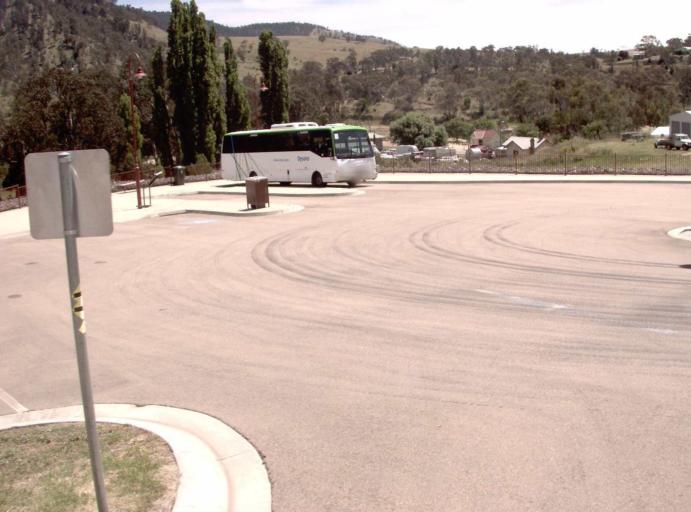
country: AU
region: Victoria
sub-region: Alpine
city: Mount Beauty
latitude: -37.1011
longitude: 147.5897
